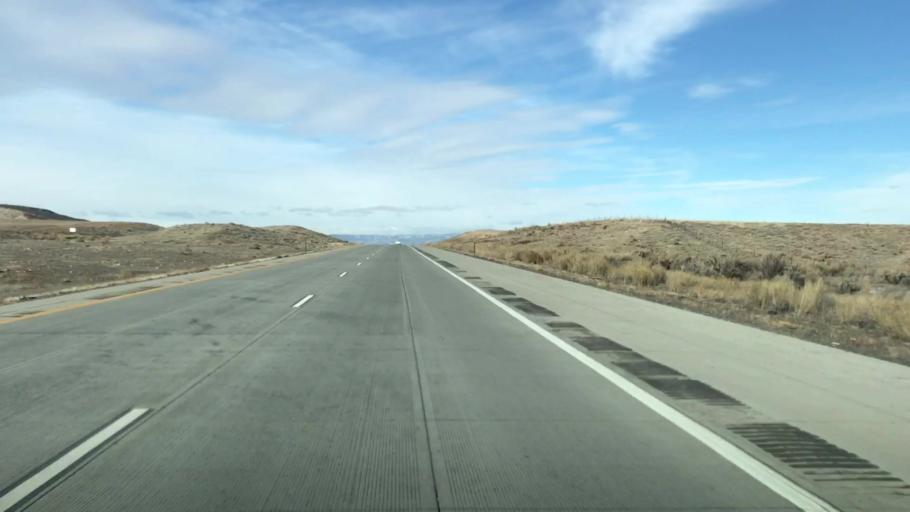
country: US
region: Colorado
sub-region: Mesa County
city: Loma
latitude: 39.1902
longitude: -108.8375
